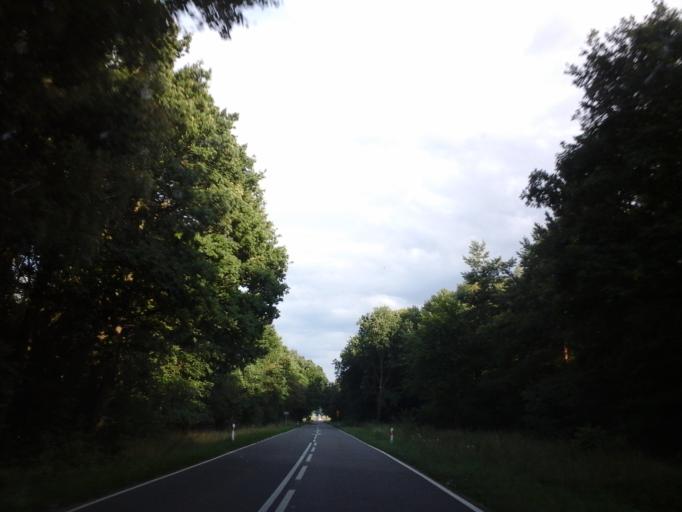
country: PL
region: West Pomeranian Voivodeship
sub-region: Powiat kamienski
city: Golczewo
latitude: 53.8763
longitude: 14.8924
